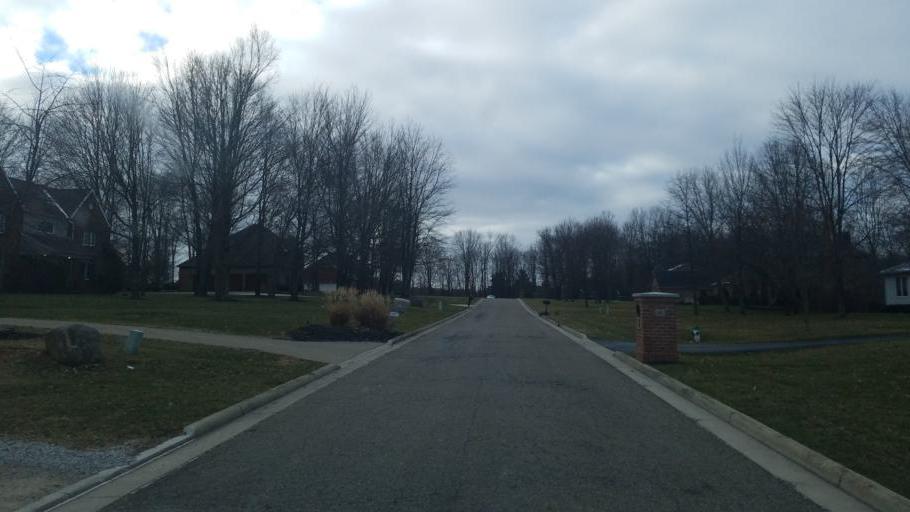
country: US
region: Ohio
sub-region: Morrow County
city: Mount Gilead
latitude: 40.5446
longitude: -82.8150
